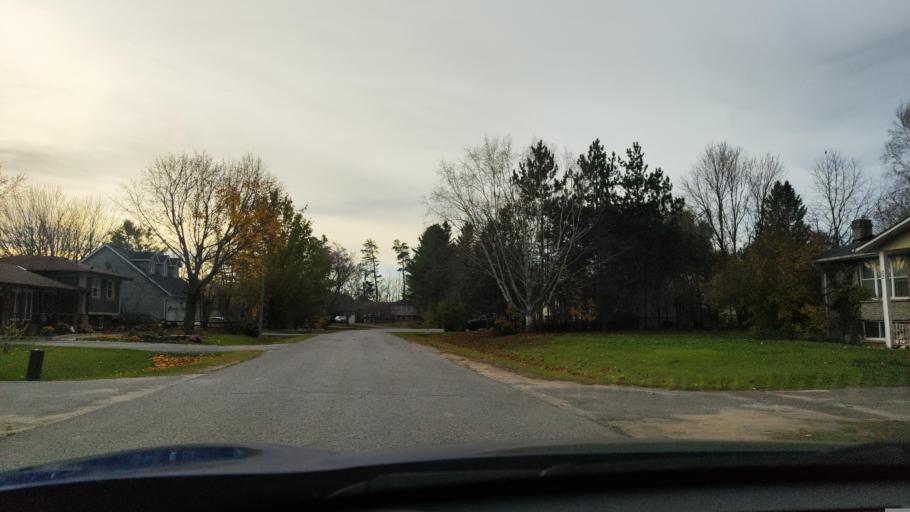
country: CA
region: Ontario
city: Angus
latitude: 44.3590
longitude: -79.9775
